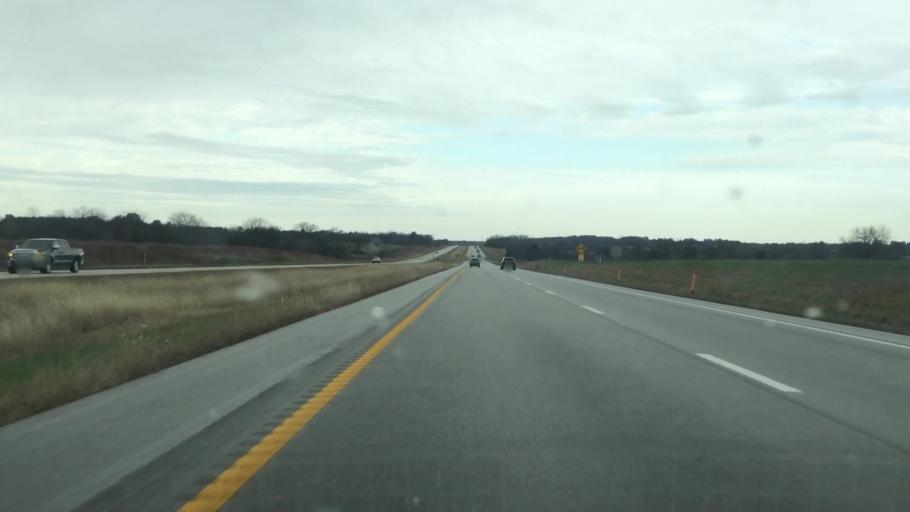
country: US
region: Missouri
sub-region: Saint Clair County
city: Osceola
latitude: 38.1917
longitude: -93.7410
